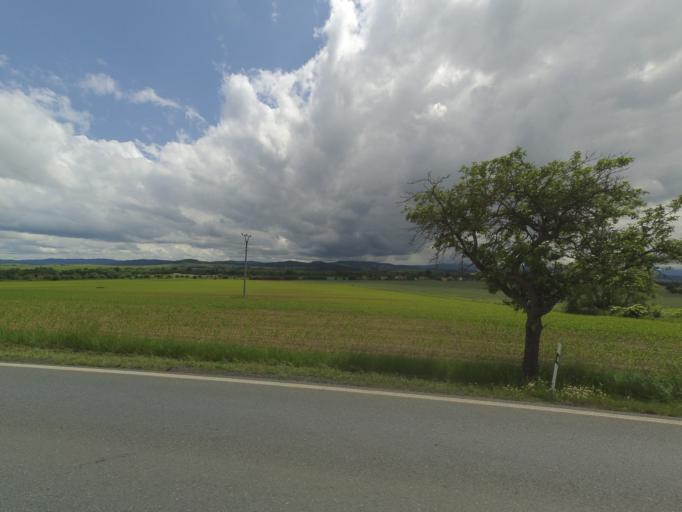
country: CZ
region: Plzensky
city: Janovice nad Uhlavou
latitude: 49.3906
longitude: 13.2427
